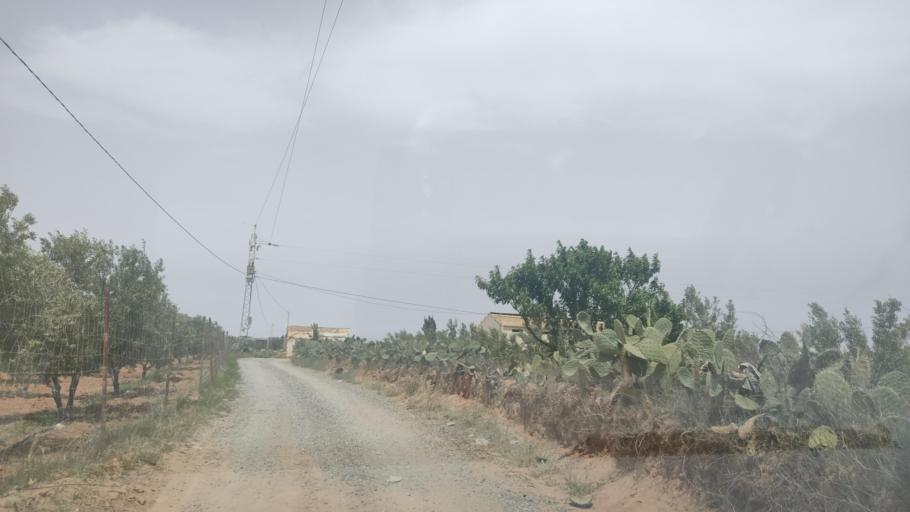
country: TN
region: Safaqis
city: Sfax
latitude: 34.8391
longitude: 10.5955
